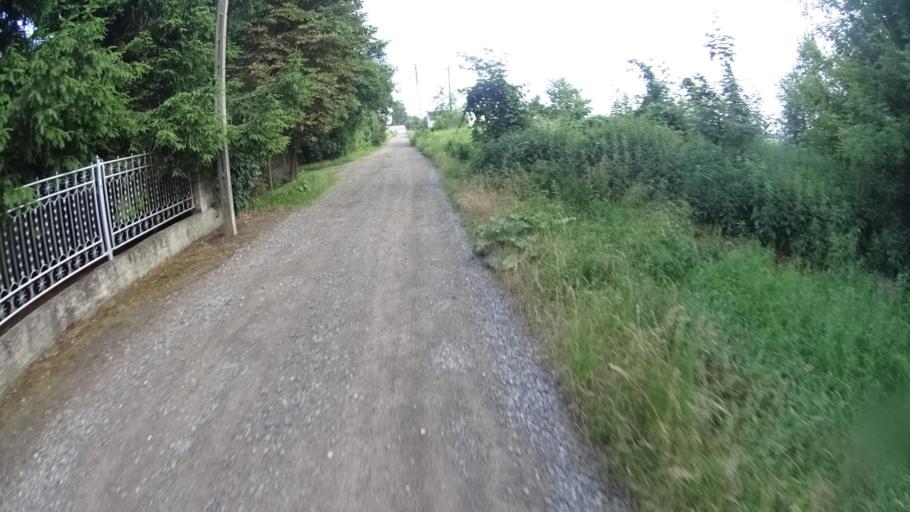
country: PL
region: Masovian Voivodeship
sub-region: Powiat warszawski zachodni
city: Babice
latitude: 52.2189
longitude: 20.8550
